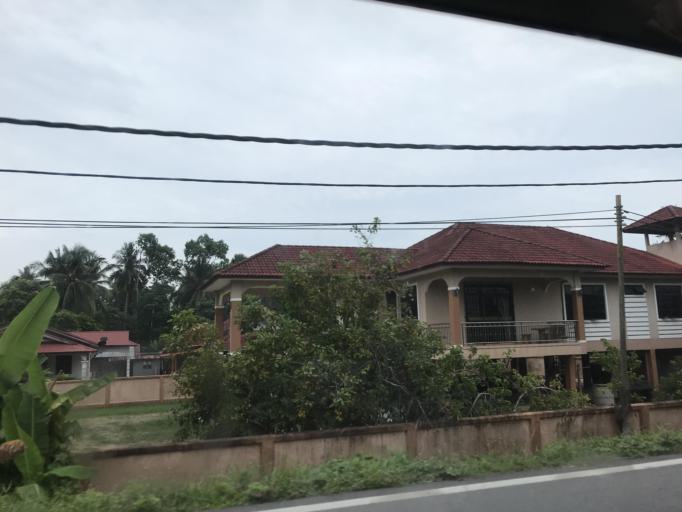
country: MY
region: Kelantan
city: Kota Bharu
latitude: 6.1614
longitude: 102.2267
